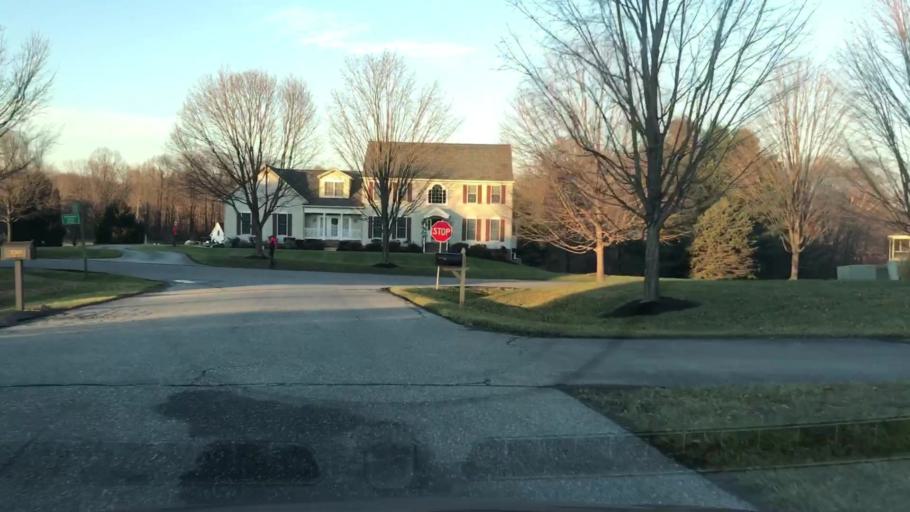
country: US
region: Maryland
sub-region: Howard County
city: Highland
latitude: 39.1807
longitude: -76.9387
